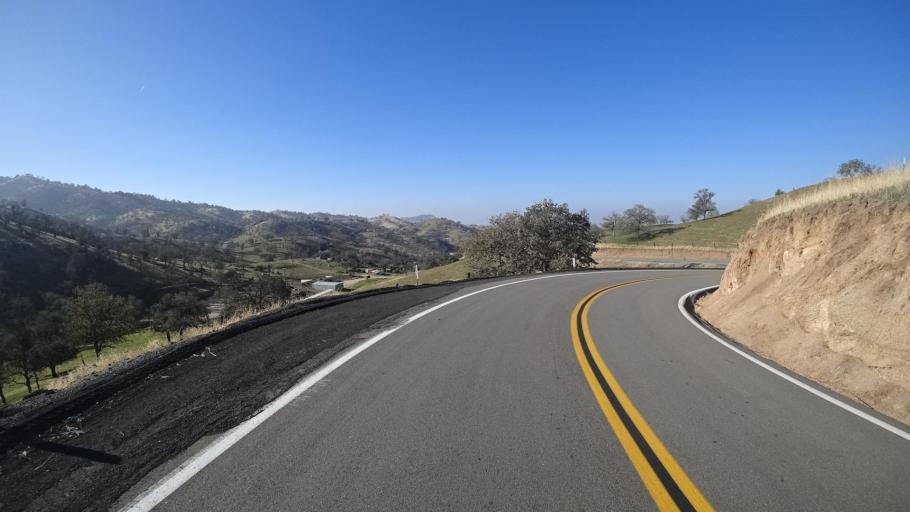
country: US
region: California
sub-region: Kern County
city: Alta Sierra
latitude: 35.7187
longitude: -118.8064
